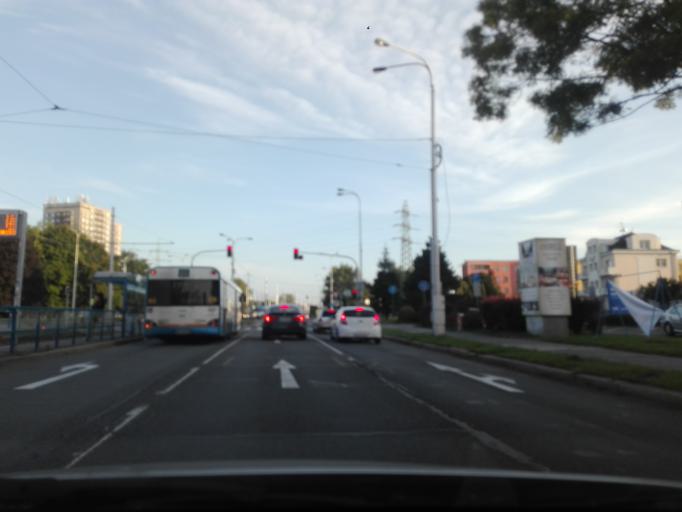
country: CZ
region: Moravskoslezsky
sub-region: Okres Ostrava-Mesto
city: Ostrava
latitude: 49.7933
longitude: 18.2505
